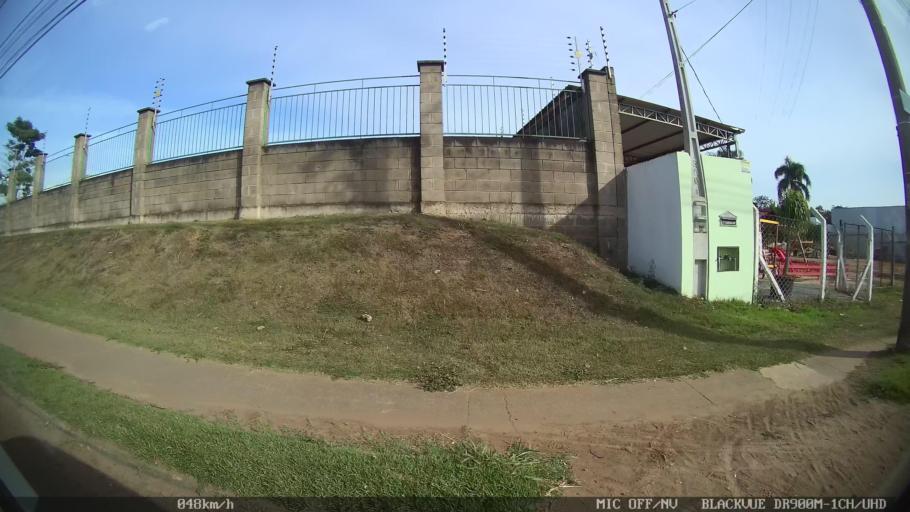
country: BR
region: Sao Paulo
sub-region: Piracicaba
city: Piracicaba
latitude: -22.7028
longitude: -47.6760
